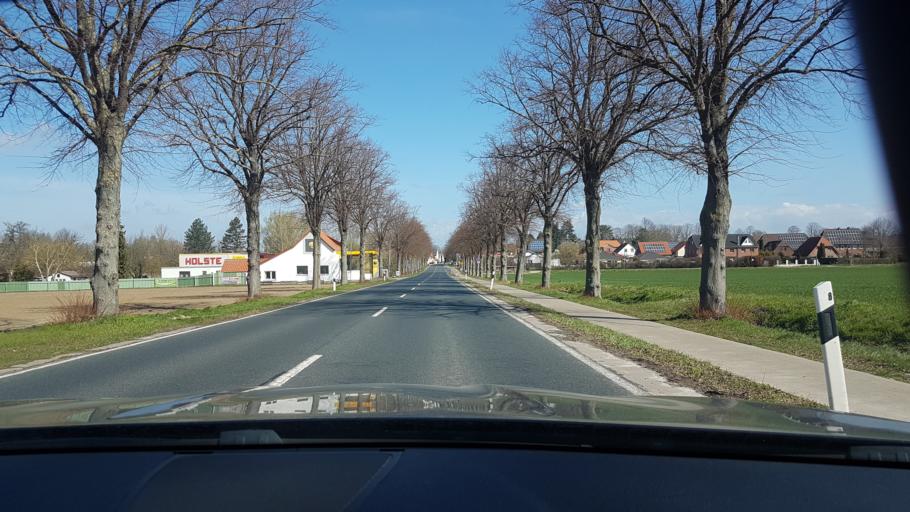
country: DE
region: Lower Saxony
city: Pattensen
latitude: 52.2553
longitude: 9.7578
